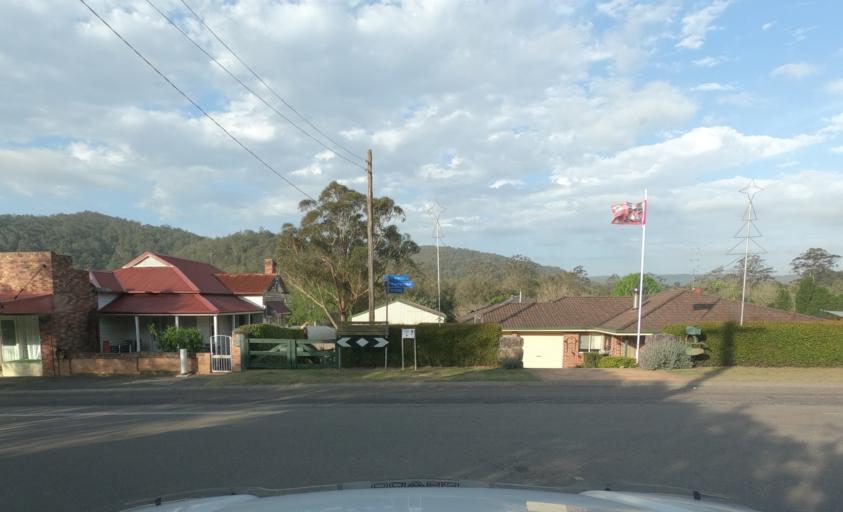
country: AU
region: New South Wales
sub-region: Wyong Shire
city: Little Jilliby
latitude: -33.2241
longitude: 151.2785
